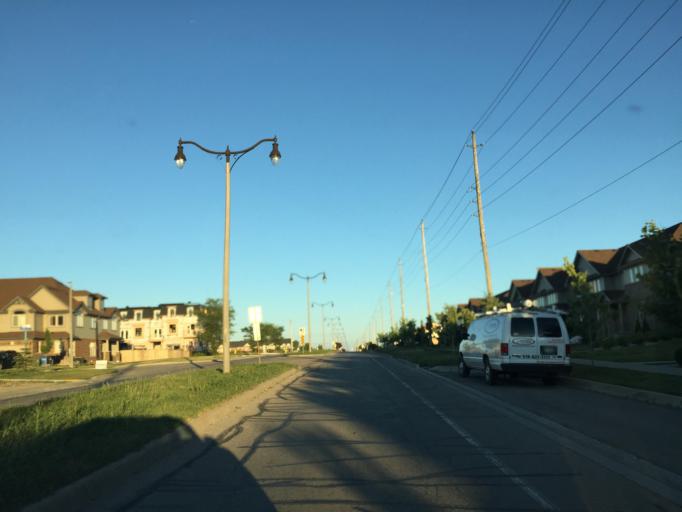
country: CA
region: Ontario
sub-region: Wellington County
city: Guelph
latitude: 43.5835
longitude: -80.2680
